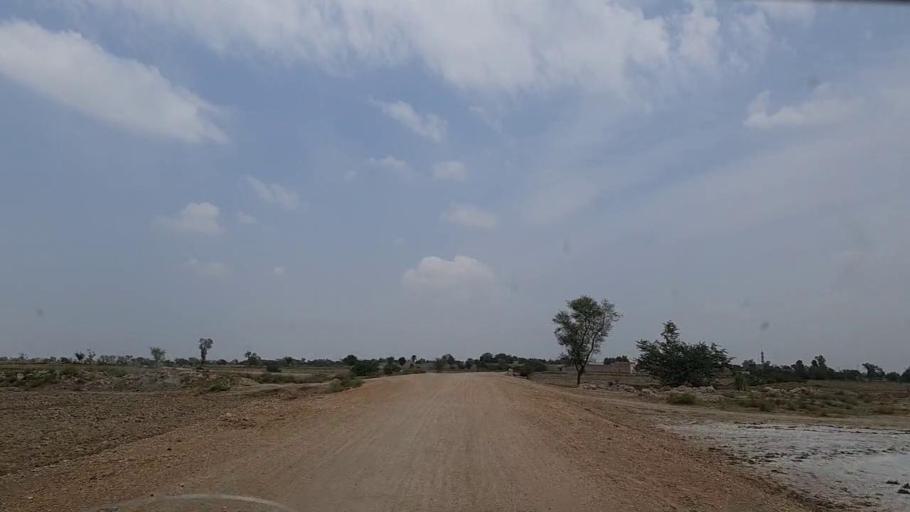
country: PK
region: Sindh
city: Phulji
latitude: 26.8230
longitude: 67.6394
